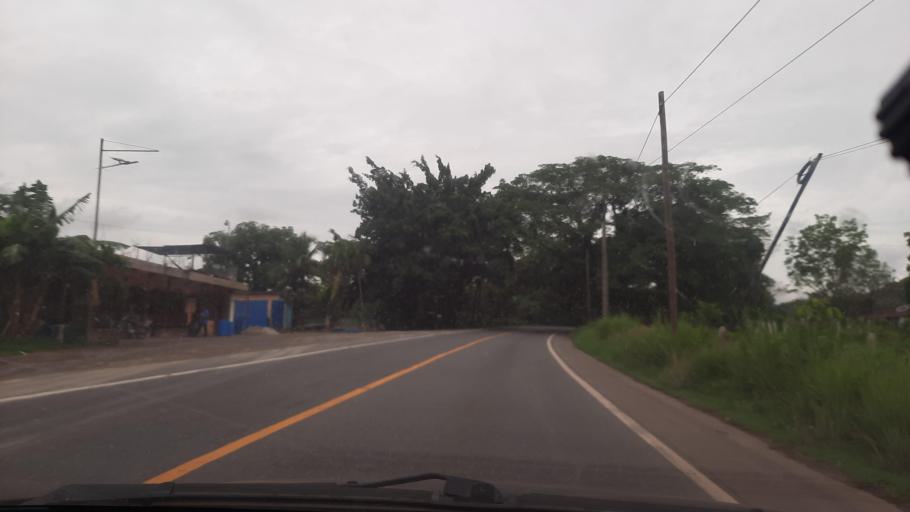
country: GT
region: Izabal
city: Morales
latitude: 15.4501
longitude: -88.9378
